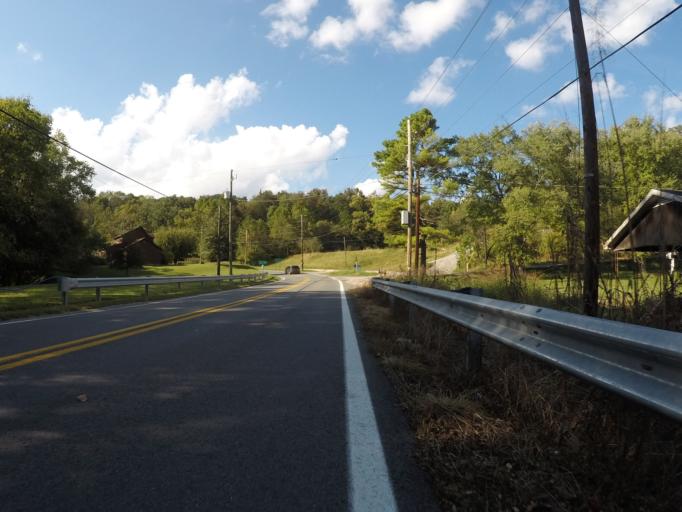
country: US
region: Ohio
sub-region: Lawrence County
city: Burlington
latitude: 38.3713
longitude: -82.5134
